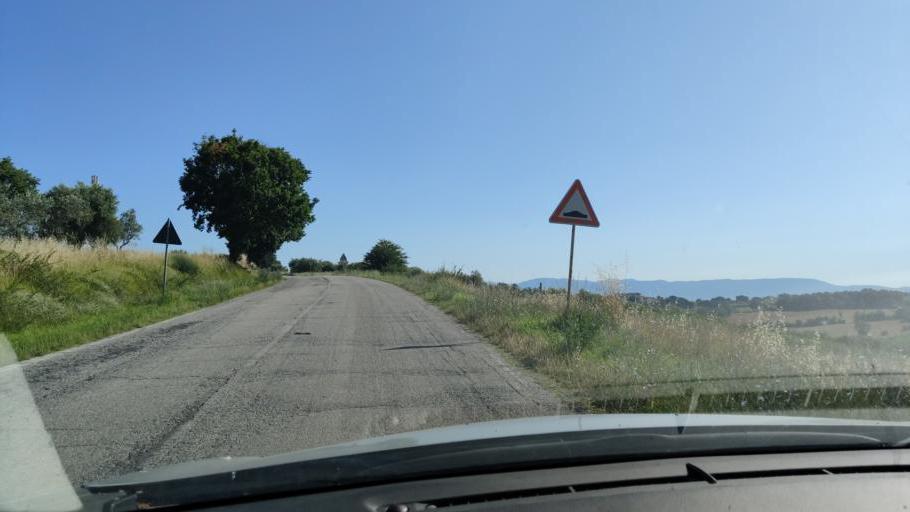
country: IT
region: Umbria
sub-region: Provincia di Terni
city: Avigliano Umbro
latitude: 42.6635
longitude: 12.4397
